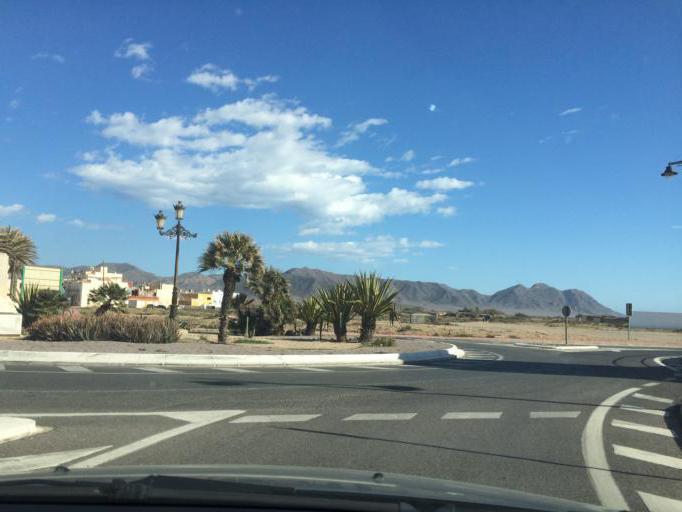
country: ES
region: Andalusia
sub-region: Provincia de Almeria
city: Retamar
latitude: 36.7808
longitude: -2.2418
